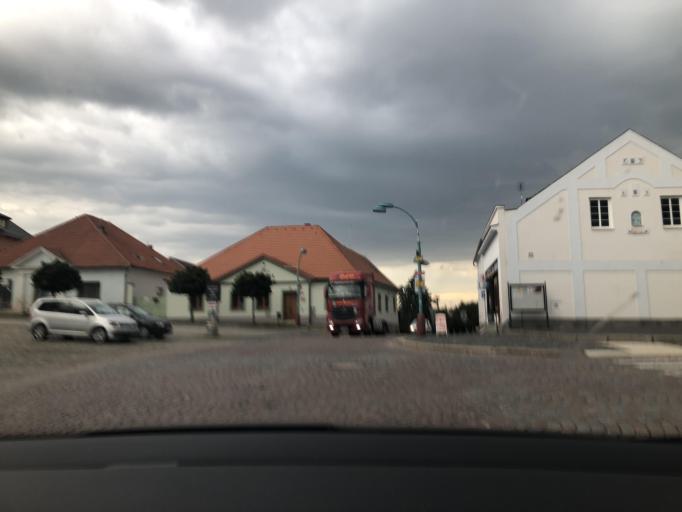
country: CZ
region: Central Bohemia
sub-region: Okres Kolin
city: Tynec nad Labem
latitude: 50.0421
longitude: 15.3579
